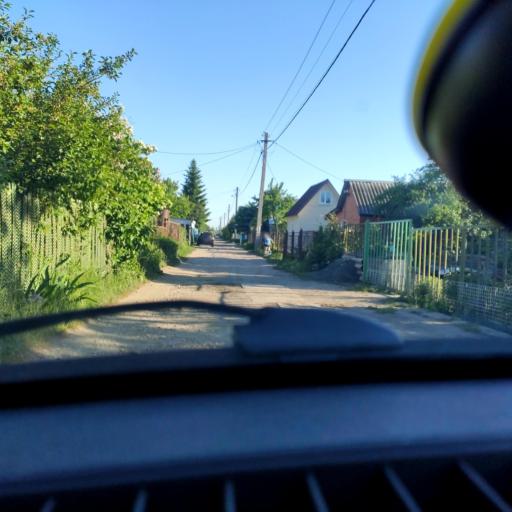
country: RU
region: Samara
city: Tol'yatti
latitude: 53.5951
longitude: 49.3157
